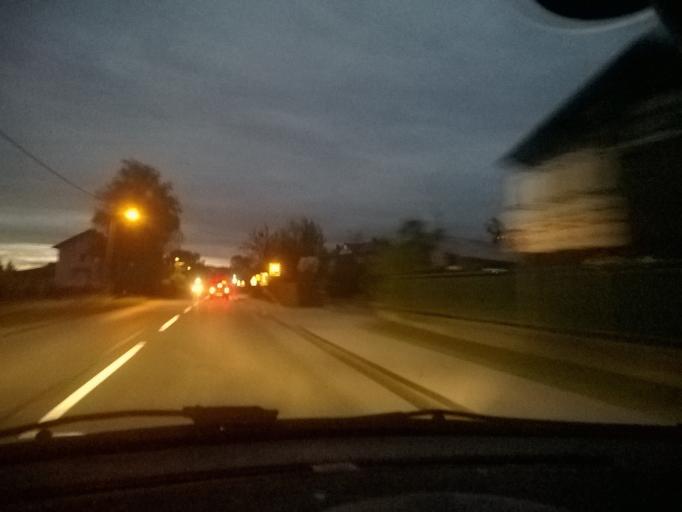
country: HR
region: Krapinsko-Zagorska
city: Zabok
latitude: 46.0622
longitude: 15.9253
